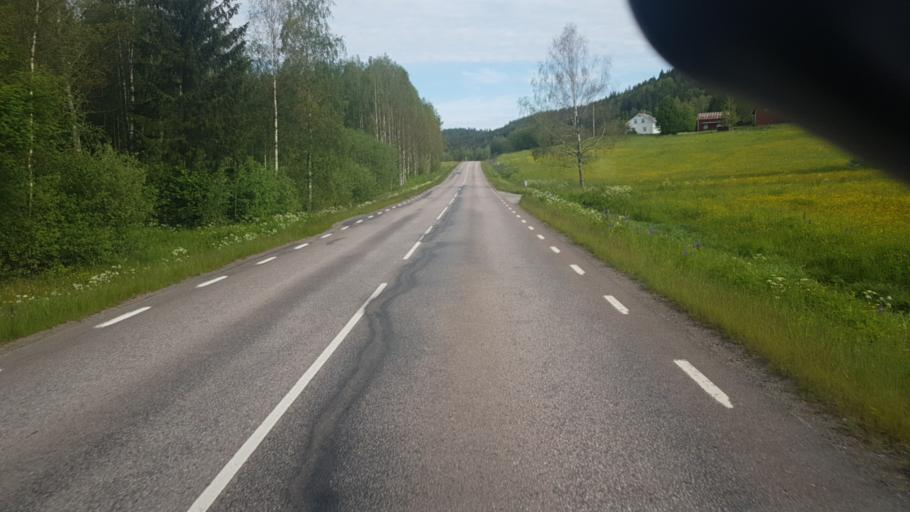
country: SE
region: Vaermland
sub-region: Arvika Kommun
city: Arvika
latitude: 59.7496
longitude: 12.6368
